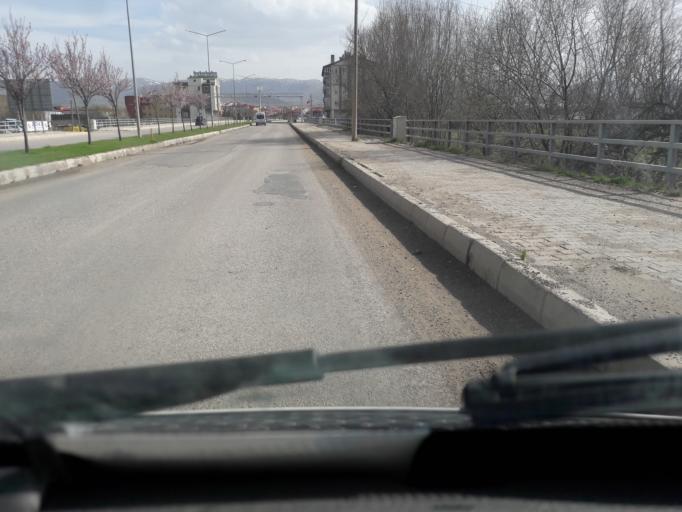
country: TR
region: Gumushane
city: Kelkit
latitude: 40.1407
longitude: 39.4334
